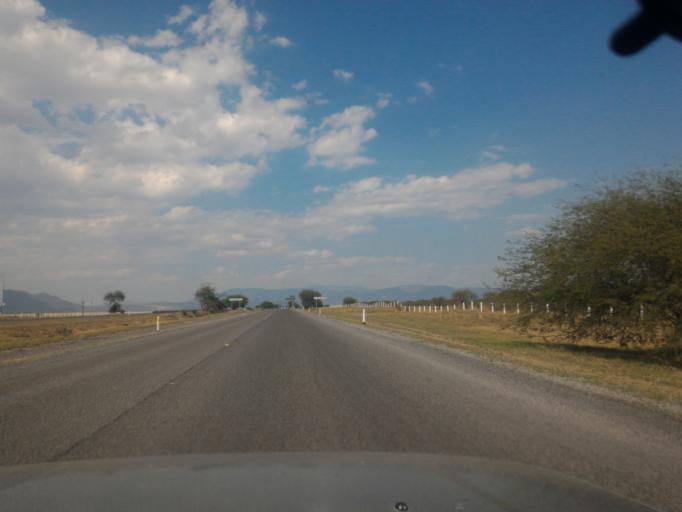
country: MX
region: Jalisco
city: Atoyac
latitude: 20.0284
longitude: -103.5293
